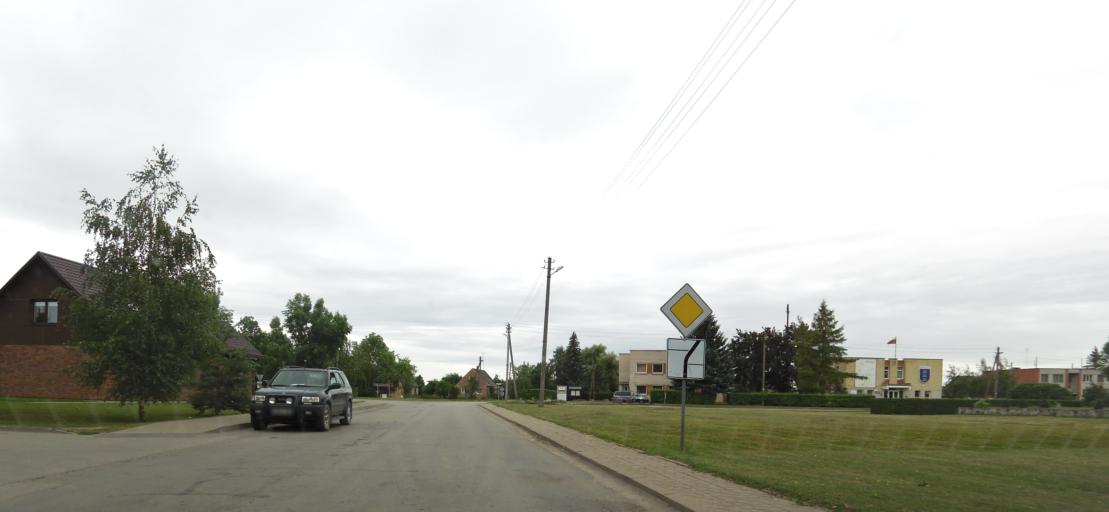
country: LT
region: Panevezys
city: Pasvalys
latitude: 56.0838
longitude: 24.5260
